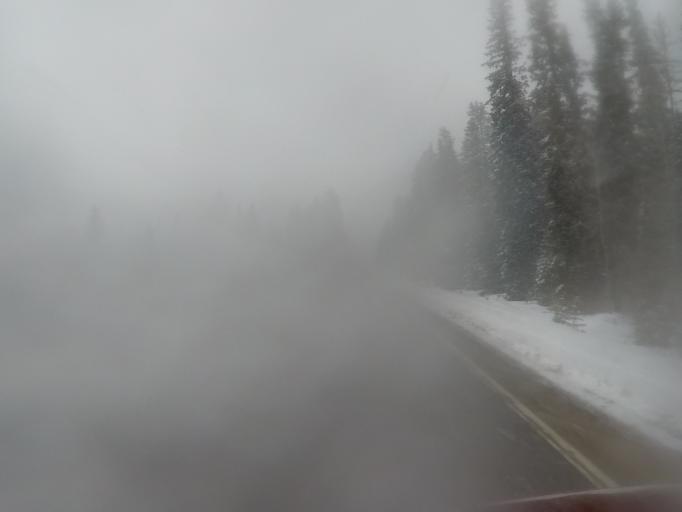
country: US
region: Montana
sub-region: Missoula County
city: Seeley Lake
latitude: 47.4327
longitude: -113.6675
